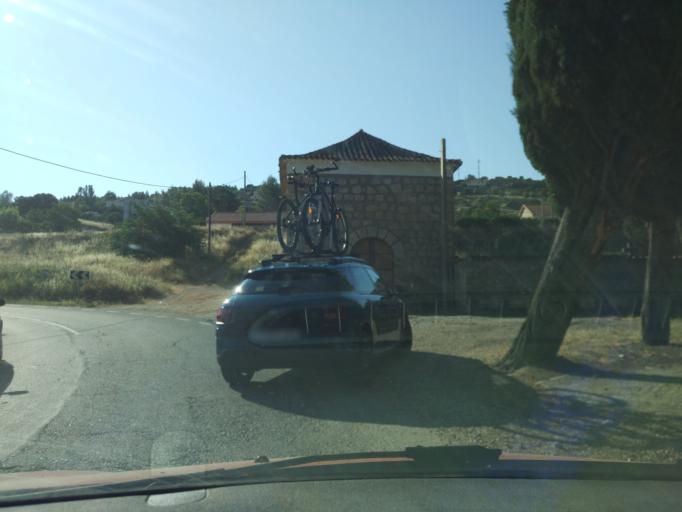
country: ES
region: Madrid
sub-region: Provincia de Madrid
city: Ambite
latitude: 40.3267
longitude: -3.1786
